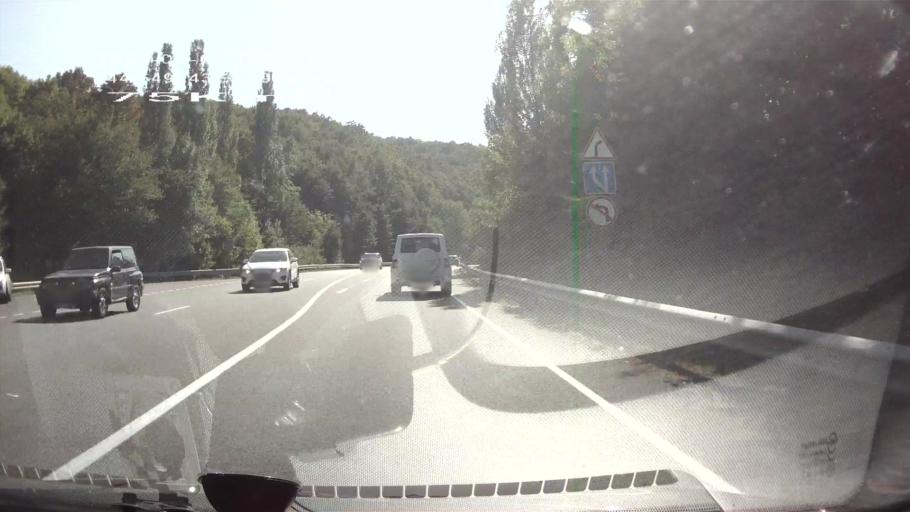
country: RU
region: Krasnodarskiy
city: Goryachiy Klyuch
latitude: 44.5491
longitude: 38.9827
